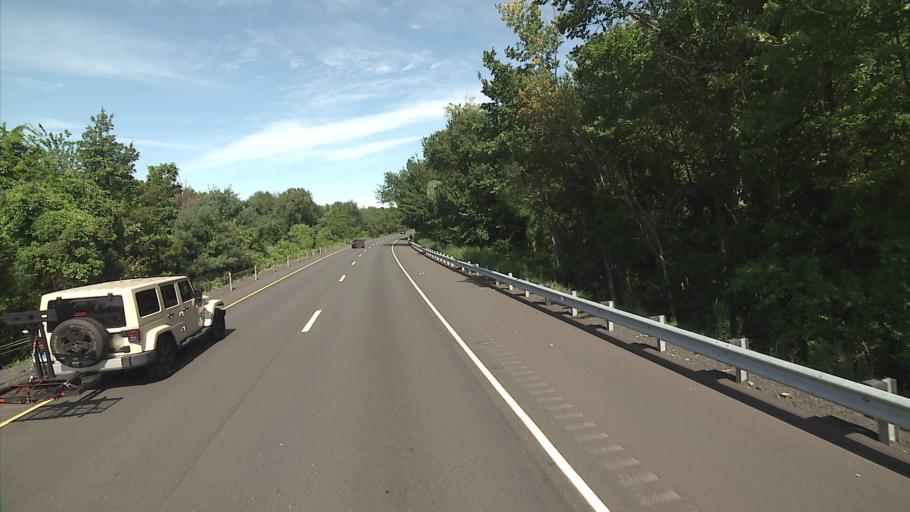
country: US
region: Connecticut
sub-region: Hartford County
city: Glastonbury Center
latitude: 41.7078
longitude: -72.5797
